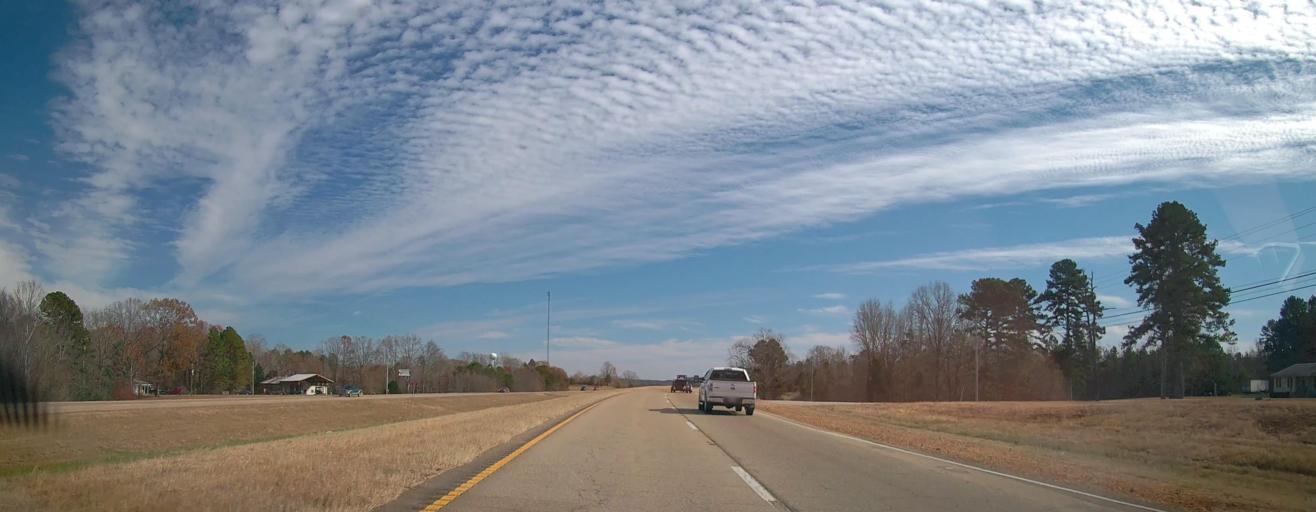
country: US
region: Mississippi
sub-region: Tippah County
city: Ripley
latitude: 34.9489
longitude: -88.8115
